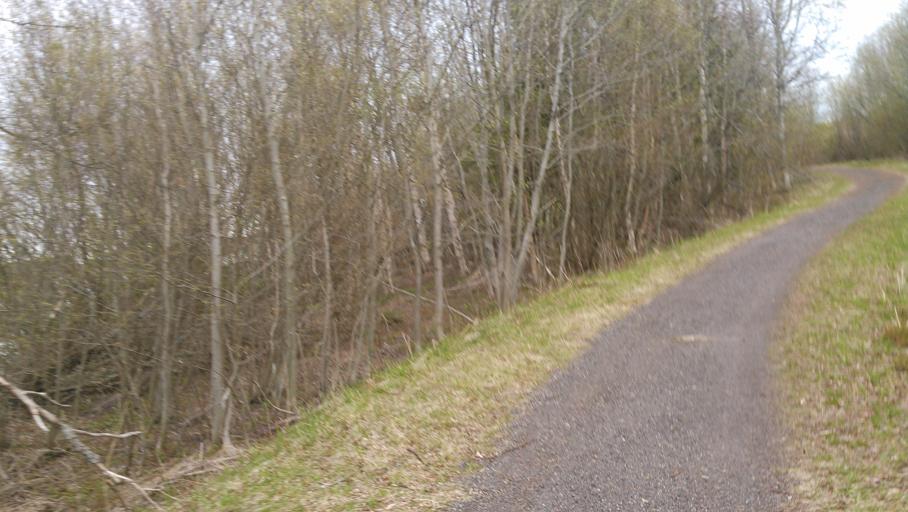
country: SE
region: Vaesterbotten
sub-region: Umea Kommun
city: Umea
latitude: 63.7849
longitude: 20.3126
